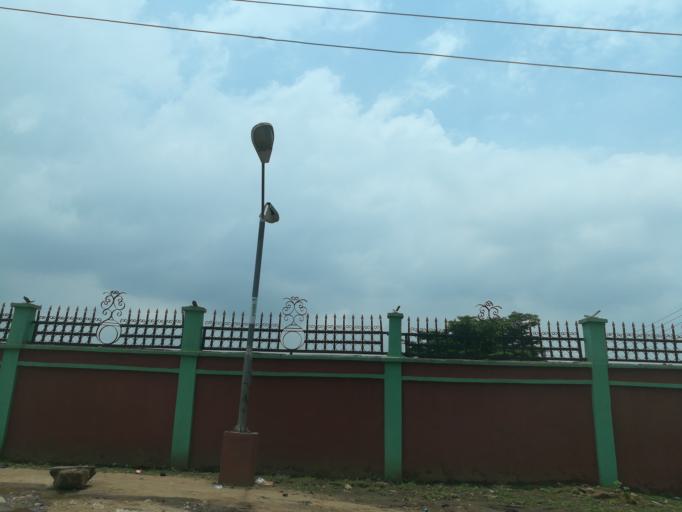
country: NG
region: Lagos
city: Ikorodu
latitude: 6.6256
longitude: 3.5510
